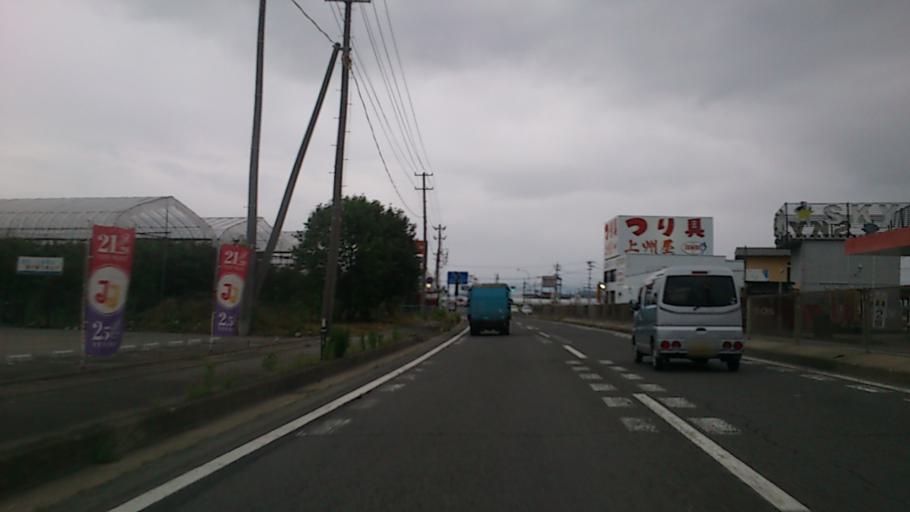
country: JP
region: Yamagata
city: Higashine
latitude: 38.4027
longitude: 140.3737
